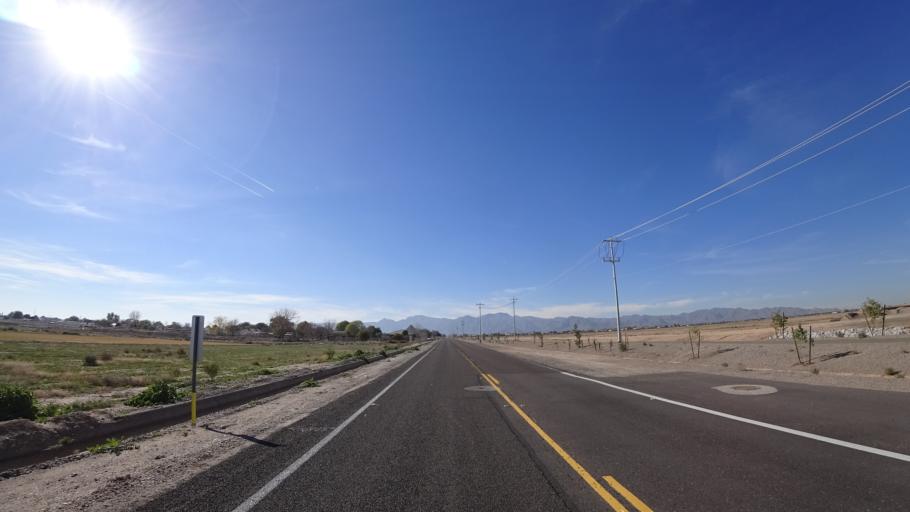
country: US
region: Arizona
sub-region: Maricopa County
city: Citrus Park
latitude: 33.5517
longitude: -112.4282
